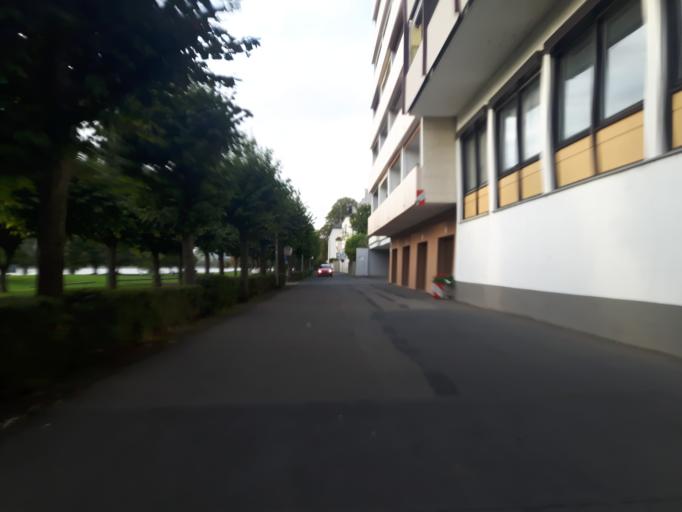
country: DE
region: Rheinland-Pfalz
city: Bad Honningen
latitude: 50.5147
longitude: 7.3059
